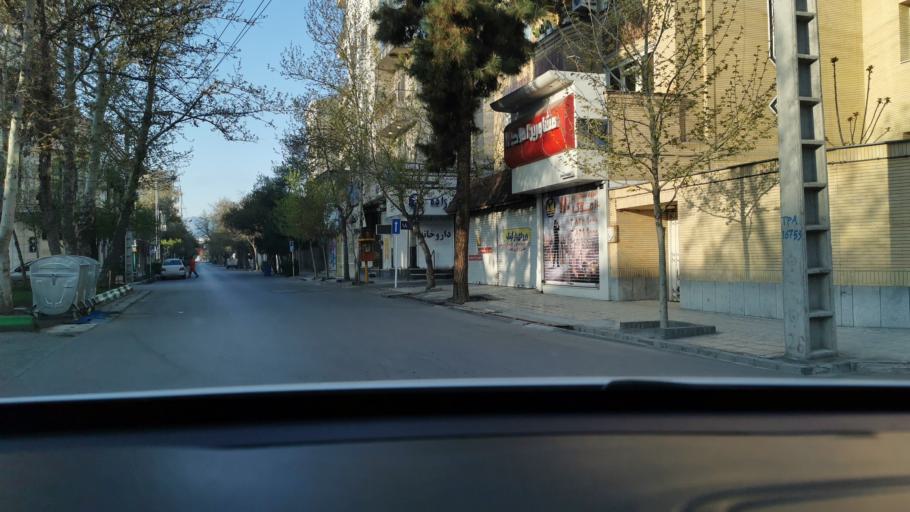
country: IR
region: Razavi Khorasan
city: Mashhad
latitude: 36.2995
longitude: 59.5807
